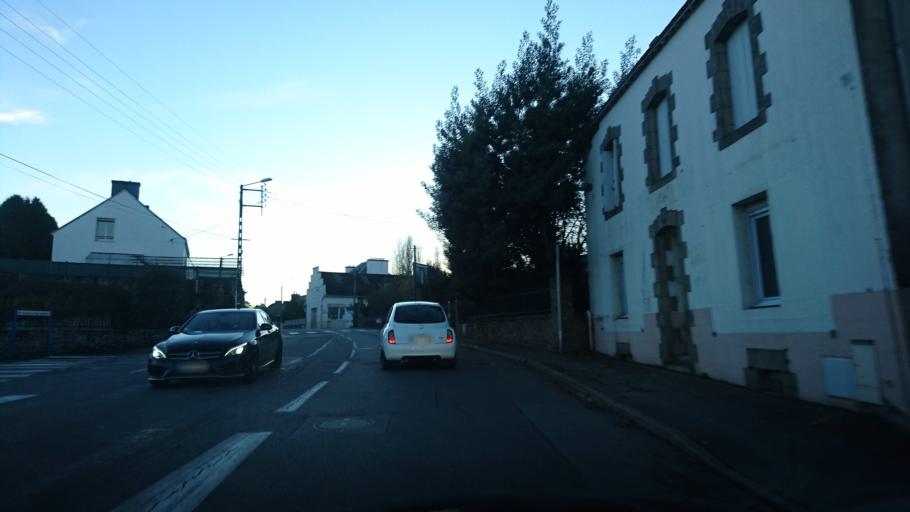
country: FR
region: Brittany
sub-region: Departement du Finistere
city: Quimperle
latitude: 47.8673
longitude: -3.5543
